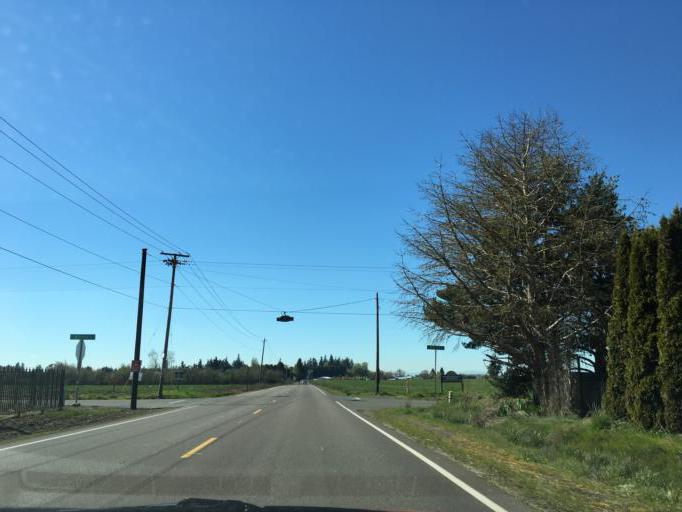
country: US
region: Oregon
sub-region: Marion County
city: Hubbard
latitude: 45.1443
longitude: -122.7567
